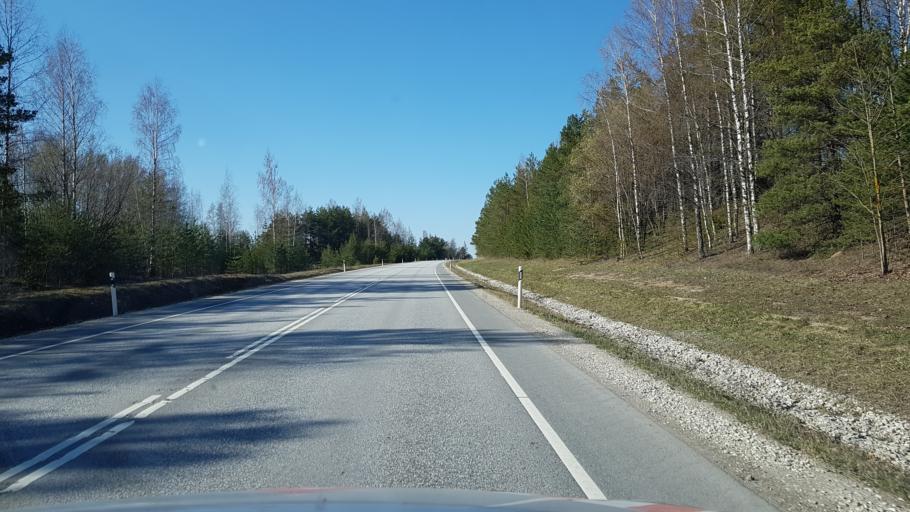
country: EE
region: Tartu
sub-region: Tartu linn
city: Tartu
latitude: 58.4789
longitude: 26.7812
